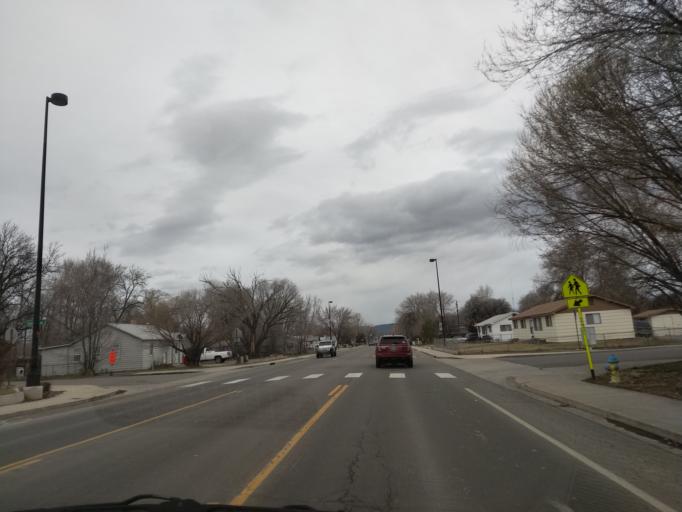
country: US
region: Colorado
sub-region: Mesa County
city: Fruitvale
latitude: 39.0822
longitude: -108.5152
